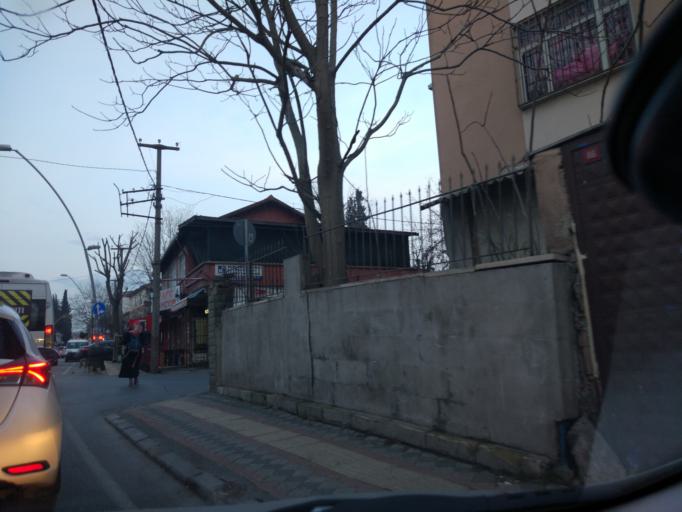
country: TR
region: Istanbul
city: Bahcelievler
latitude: 41.0105
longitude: 28.8228
